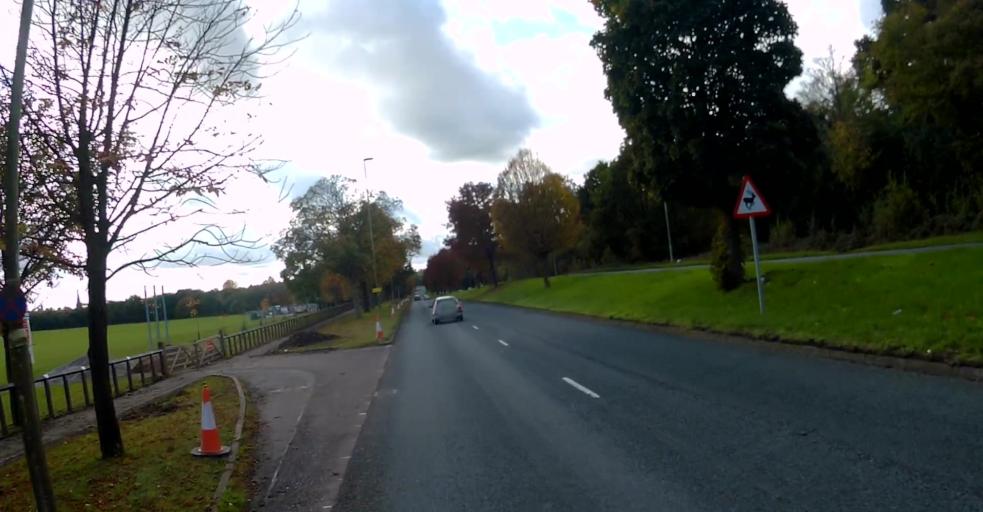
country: GB
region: England
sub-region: Hampshire
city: Aldershot
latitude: 51.2684
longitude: -0.7609
